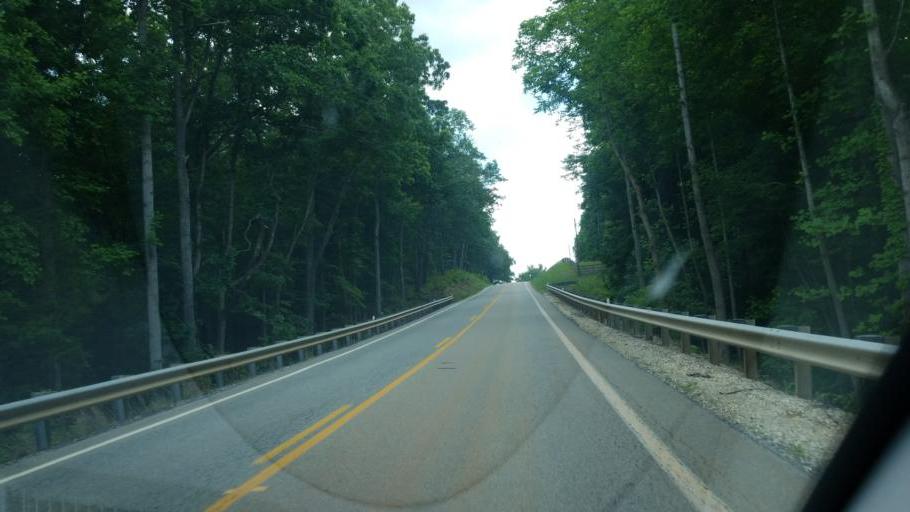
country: US
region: Virginia
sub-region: Buckingham County
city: Buckingham
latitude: 37.5306
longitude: -78.7134
